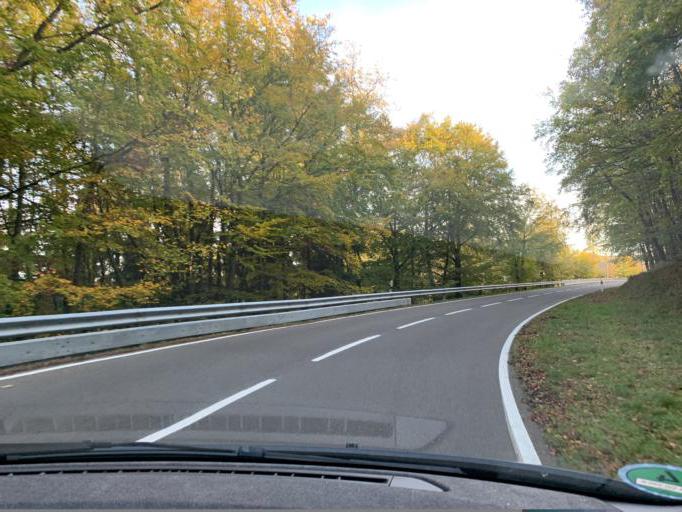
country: DE
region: North Rhine-Westphalia
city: Heimbach
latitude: 50.6082
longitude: 6.4810
